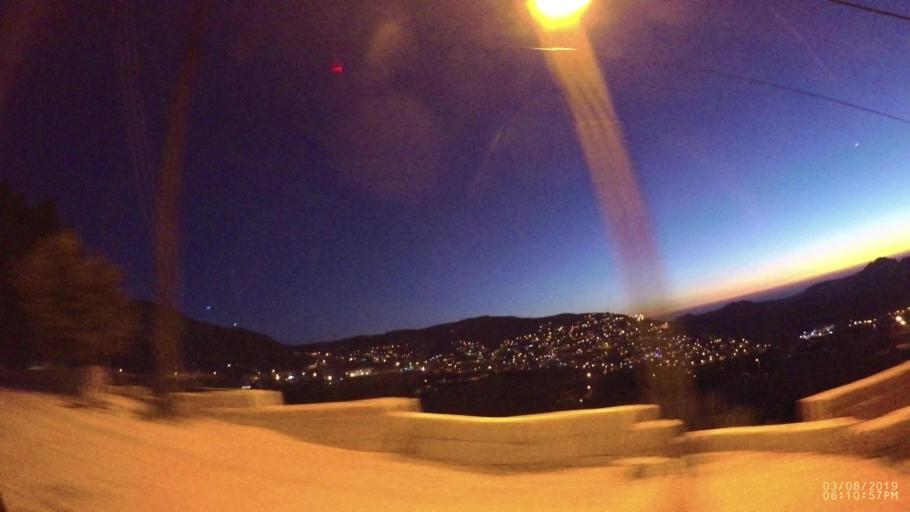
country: JO
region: Ma'an
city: Petra
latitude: 30.3302
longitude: 35.4875
